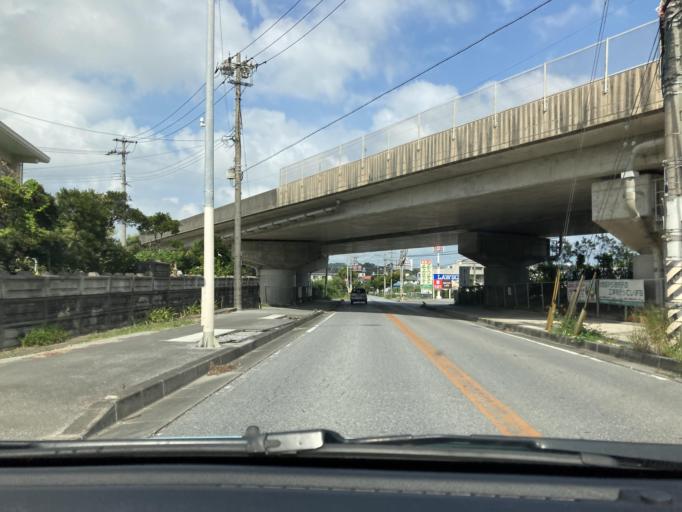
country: JP
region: Okinawa
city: Ginowan
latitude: 26.2297
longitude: 127.7386
